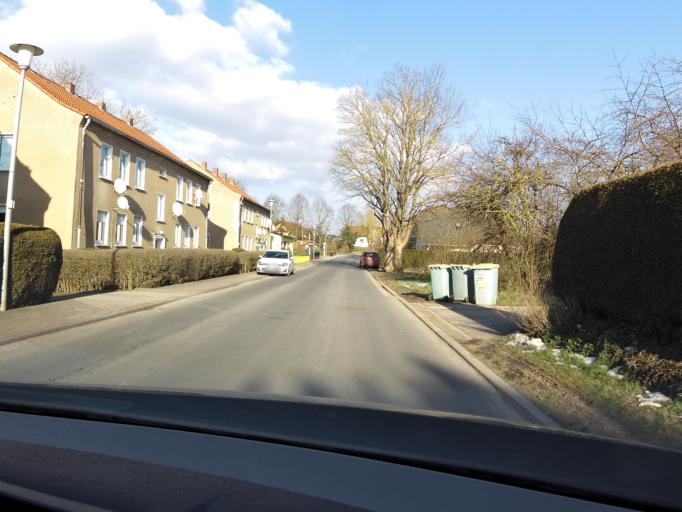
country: DE
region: Thuringia
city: Leimbach
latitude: 50.8449
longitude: 10.2130
